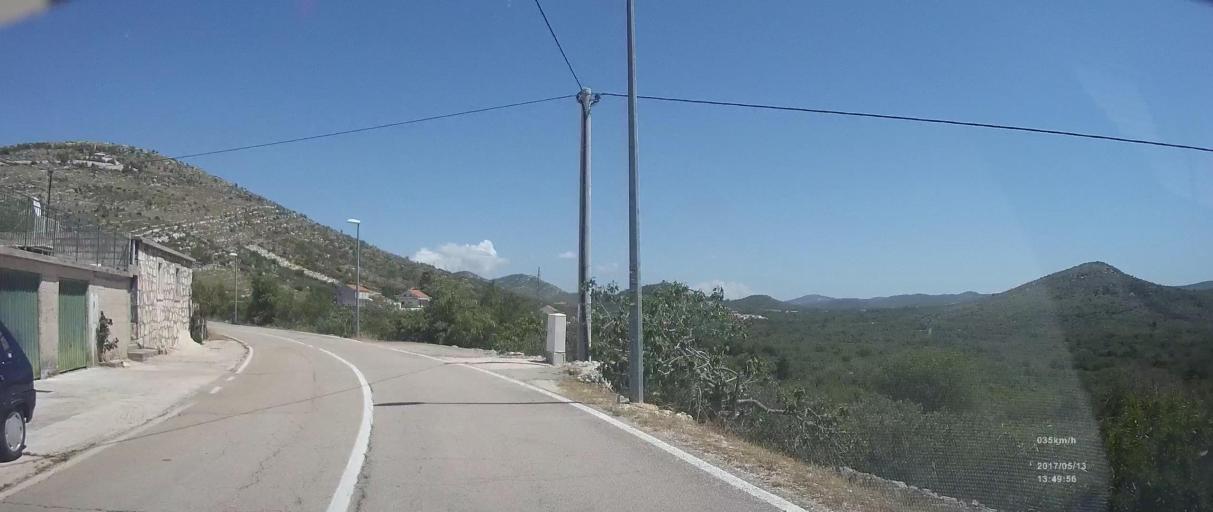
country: HR
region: Sibensko-Kniniska
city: Primosten
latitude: 43.6113
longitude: 15.9789
